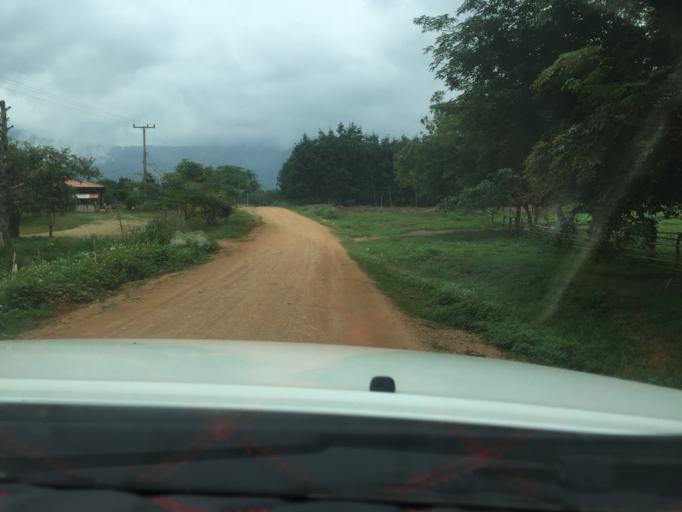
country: TH
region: Phayao
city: Phu Sang
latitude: 19.7393
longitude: 100.4659
